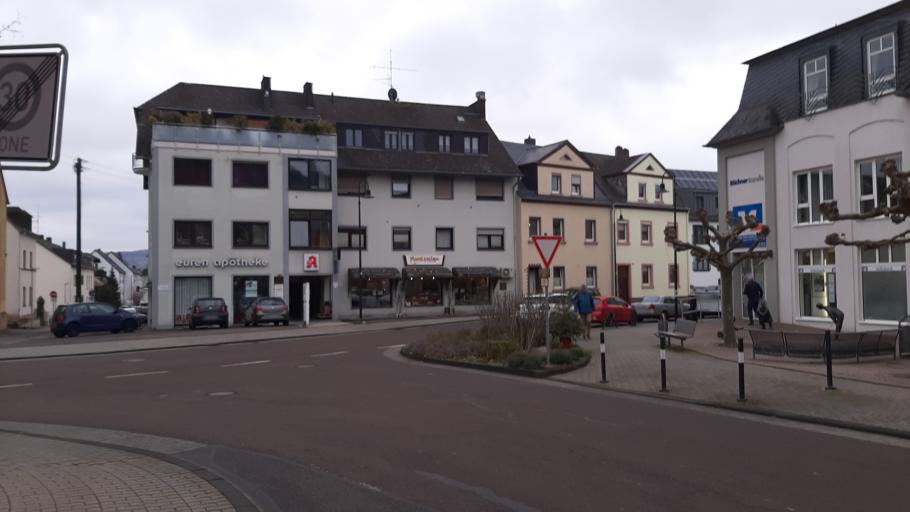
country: DE
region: Rheinland-Pfalz
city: Trier
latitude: 49.7406
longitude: 6.6090
